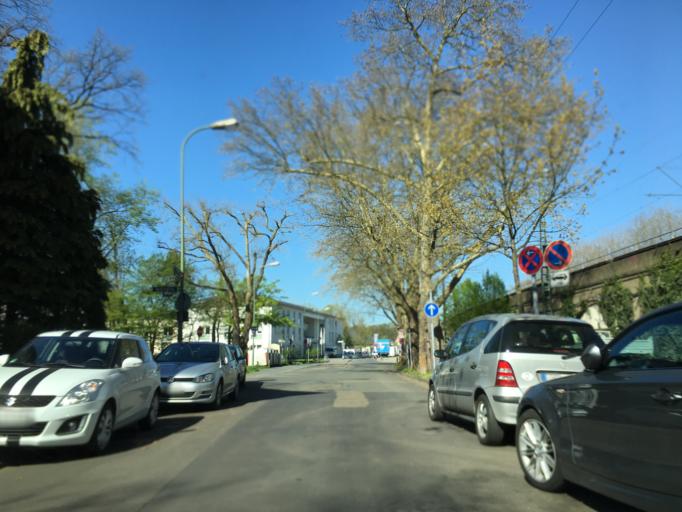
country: DE
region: Hesse
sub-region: Regierungsbezirk Darmstadt
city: Offenbach
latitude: 50.0981
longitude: 8.7525
